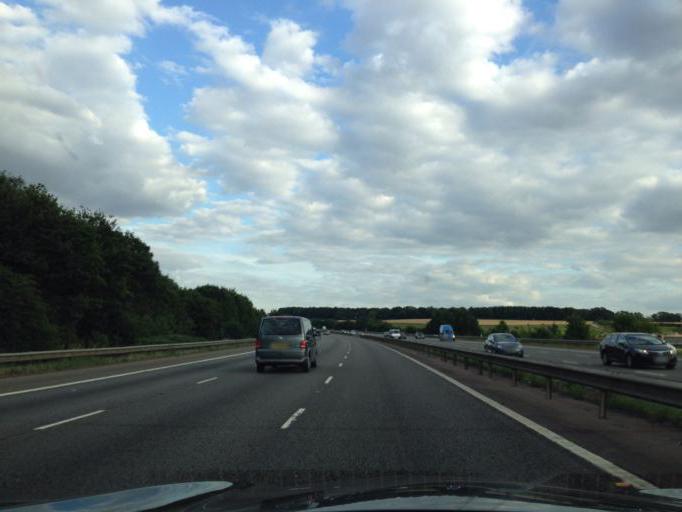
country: GB
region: England
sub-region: Oxfordshire
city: Somerton
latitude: 51.9724
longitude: -1.2578
